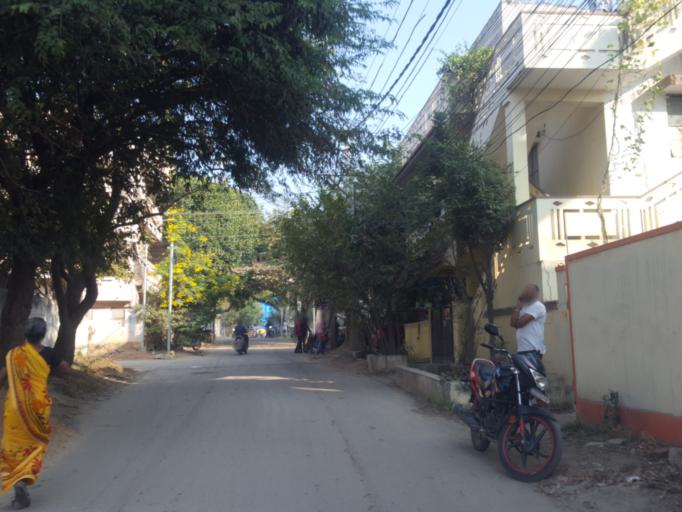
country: IN
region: Telangana
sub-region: Rangareddi
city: Kukatpalli
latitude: 17.4459
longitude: 78.3587
